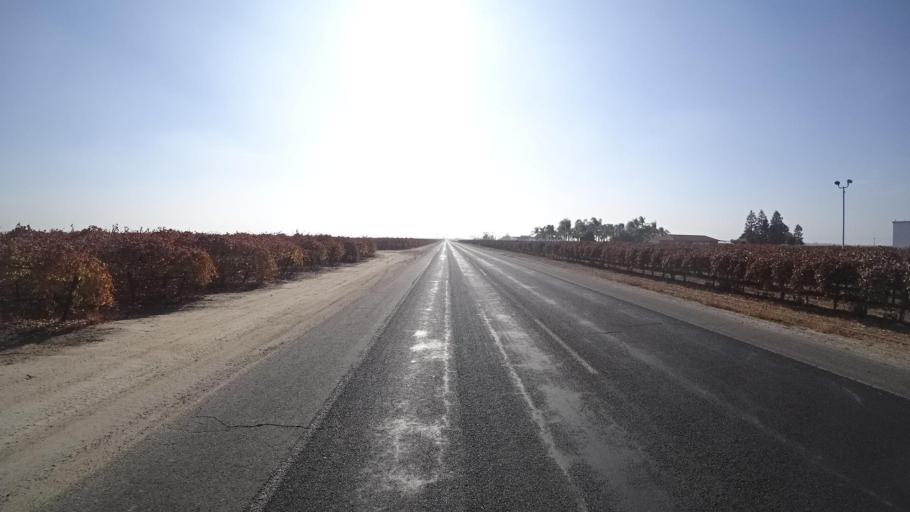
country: US
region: California
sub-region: Kern County
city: McFarland
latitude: 35.6811
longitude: -119.1824
